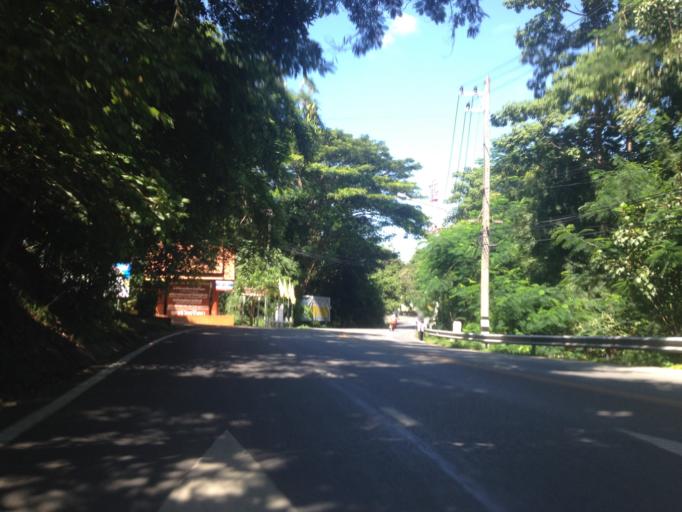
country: TH
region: Chiang Mai
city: Chiang Mai
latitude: 18.8144
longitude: 98.9465
